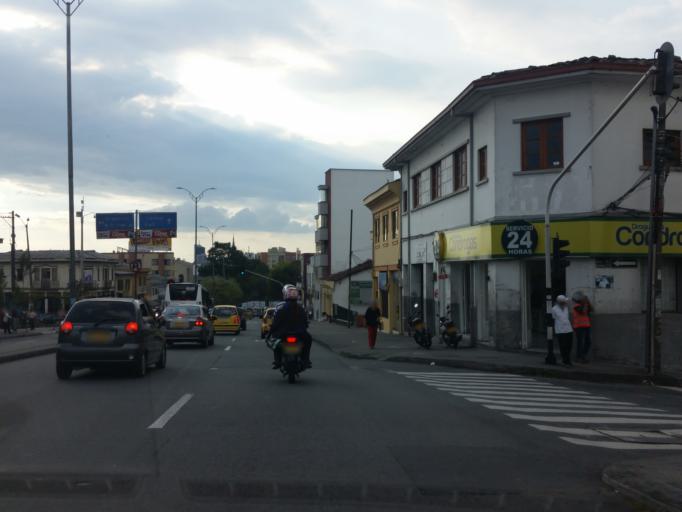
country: CO
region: Caldas
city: Manizales
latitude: 5.0656
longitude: -75.5019
